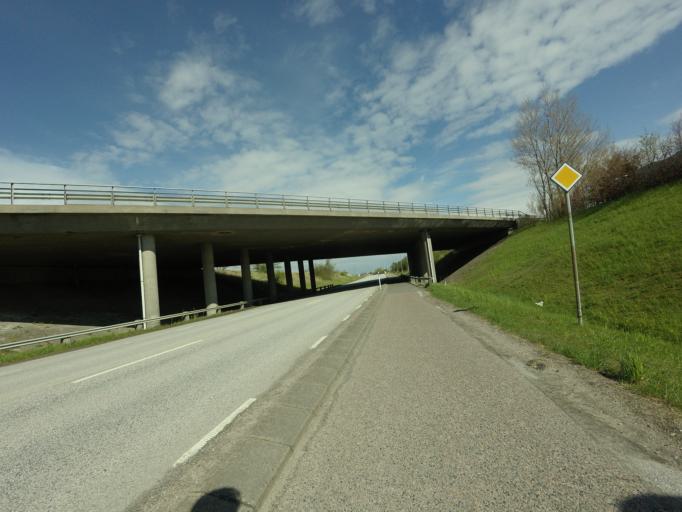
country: SE
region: Skane
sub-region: Vellinge Kommun
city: Vellinge
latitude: 55.4797
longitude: 13.0156
